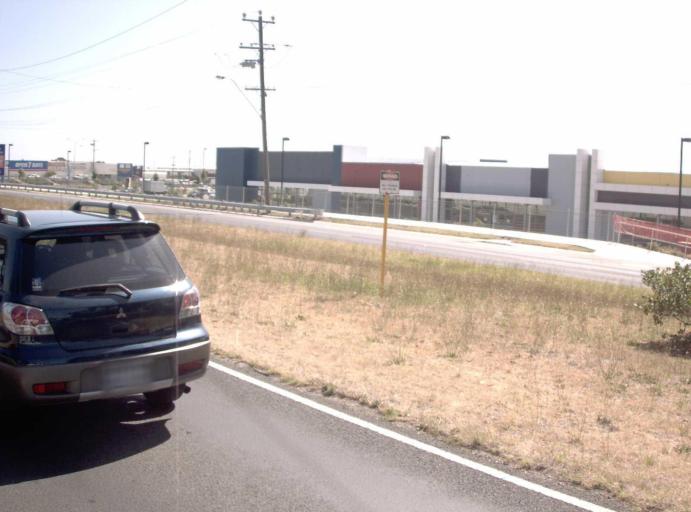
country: AU
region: Victoria
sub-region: Frankston
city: Carrum Downs
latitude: -38.0980
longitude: 145.1740
